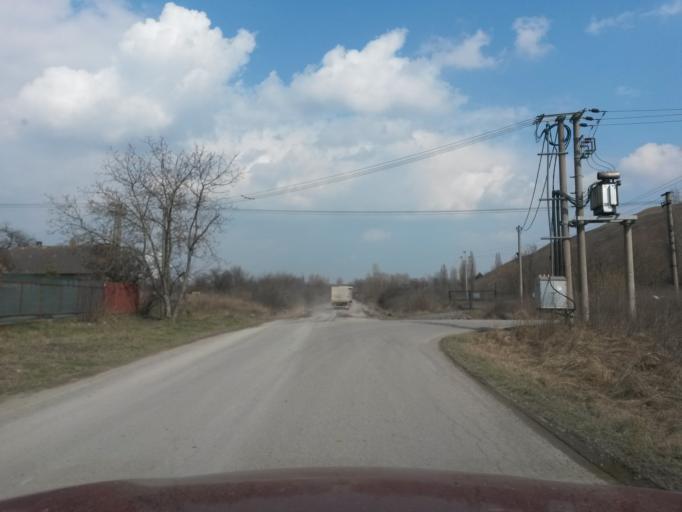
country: SK
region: Kosicky
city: Kosice
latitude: 48.5891
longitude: 21.1737
